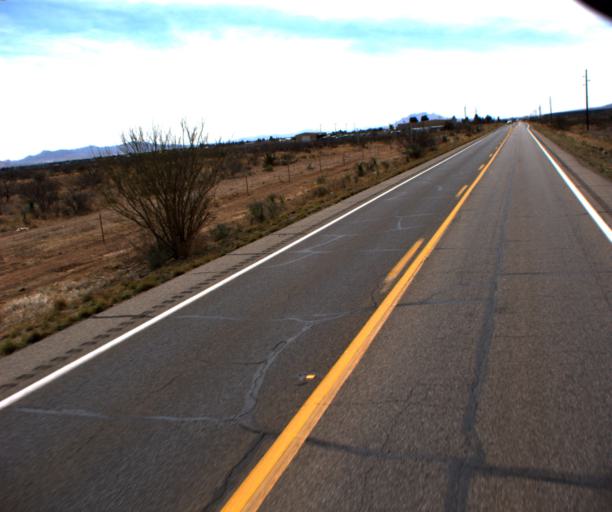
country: US
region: Arizona
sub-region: Cochise County
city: Pirtleville
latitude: 31.3753
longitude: -109.5794
